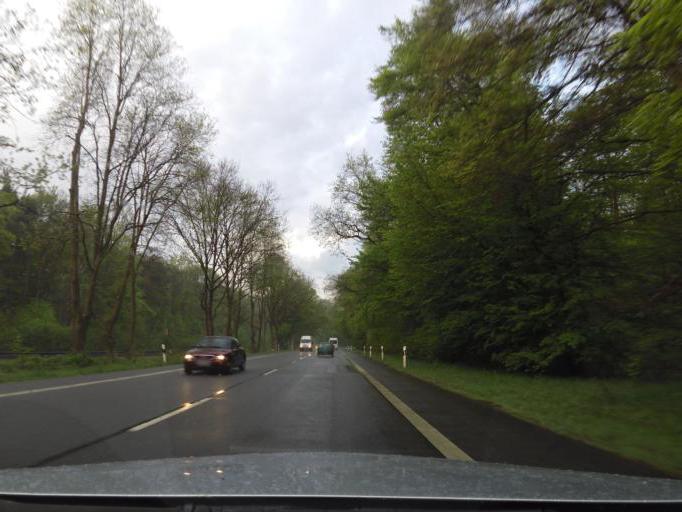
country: DE
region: Hesse
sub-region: Regierungsbezirk Darmstadt
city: Buttelborn
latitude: 49.9535
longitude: 8.5366
